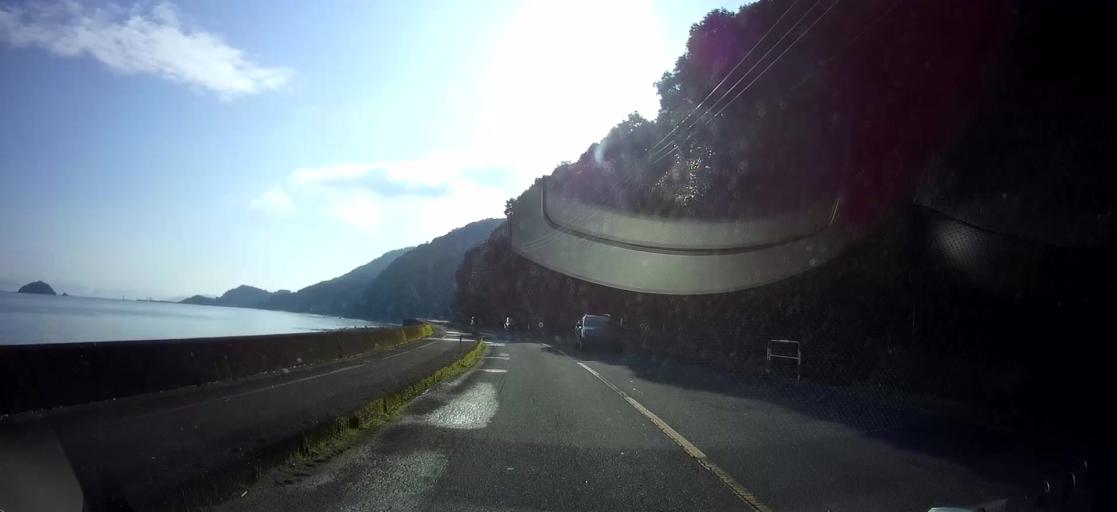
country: JP
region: Kumamoto
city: Yatsushiro
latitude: 32.4886
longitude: 130.4389
